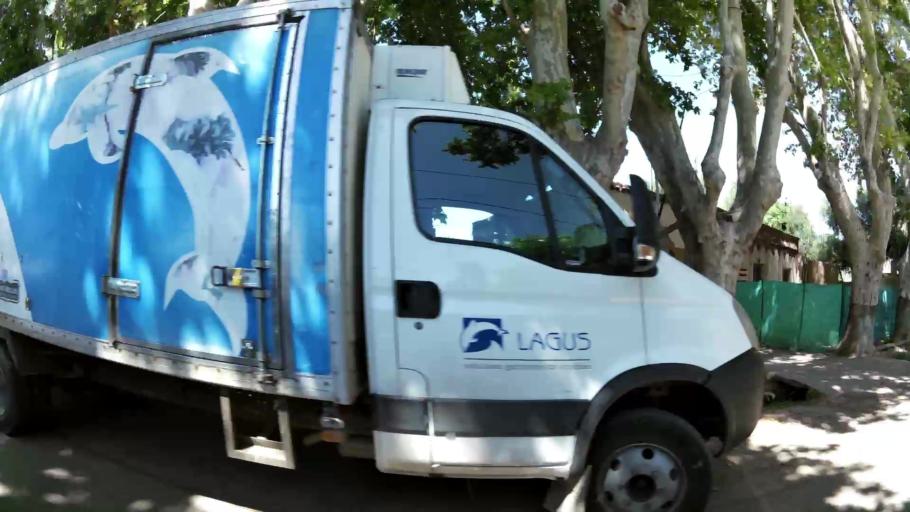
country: AR
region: Mendoza
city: Las Heras
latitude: -32.8680
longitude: -68.7997
